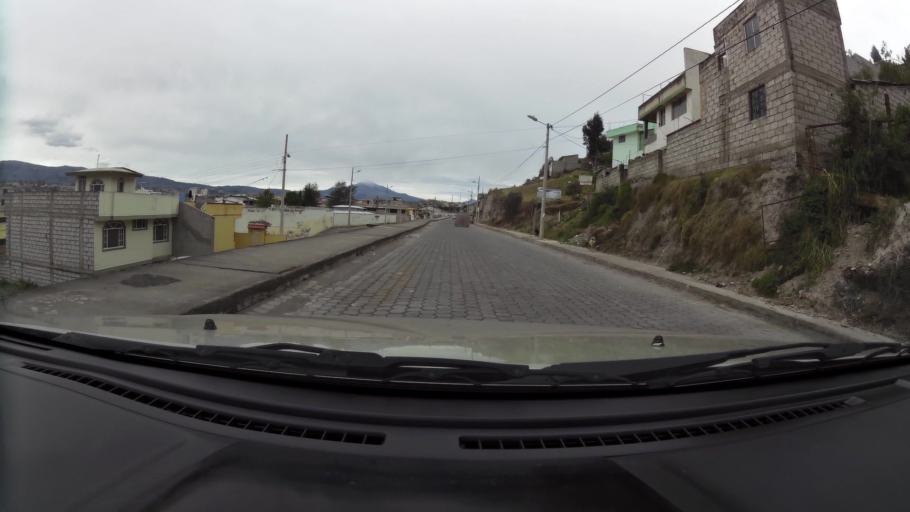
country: EC
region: Cotopaxi
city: Latacunga
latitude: -0.9375
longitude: -78.6102
